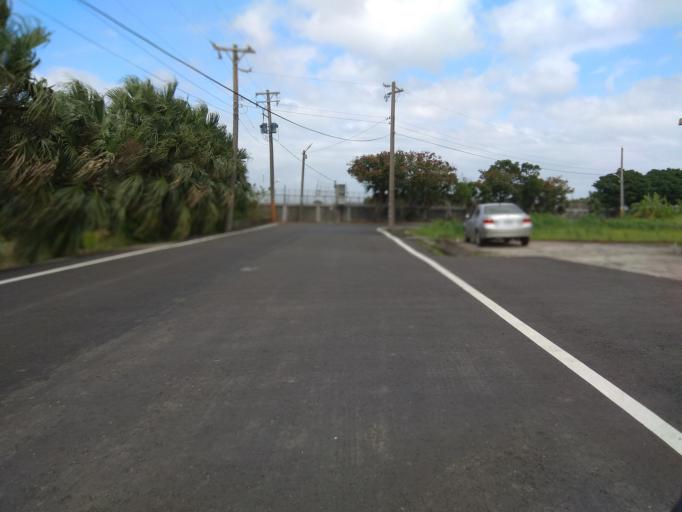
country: TW
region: Taiwan
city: Taoyuan City
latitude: 25.0635
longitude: 121.2309
